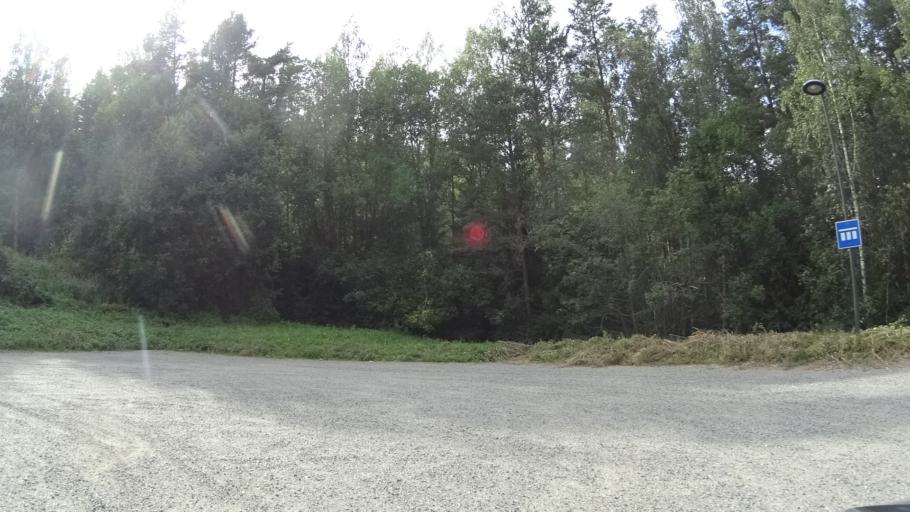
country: FI
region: Pirkanmaa
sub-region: Etelae-Pirkanmaa
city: Valkeakoski
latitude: 61.2052
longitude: 24.0621
